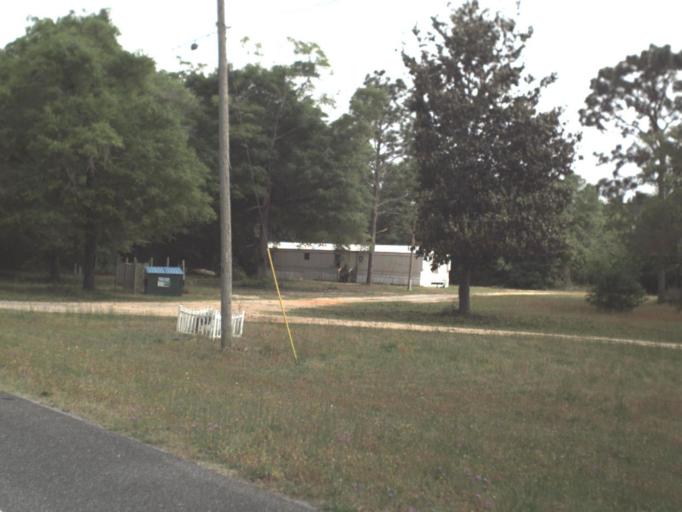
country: US
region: Florida
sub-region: Santa Rosa County
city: Point Baker
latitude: 30.7007
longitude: -87.0753
